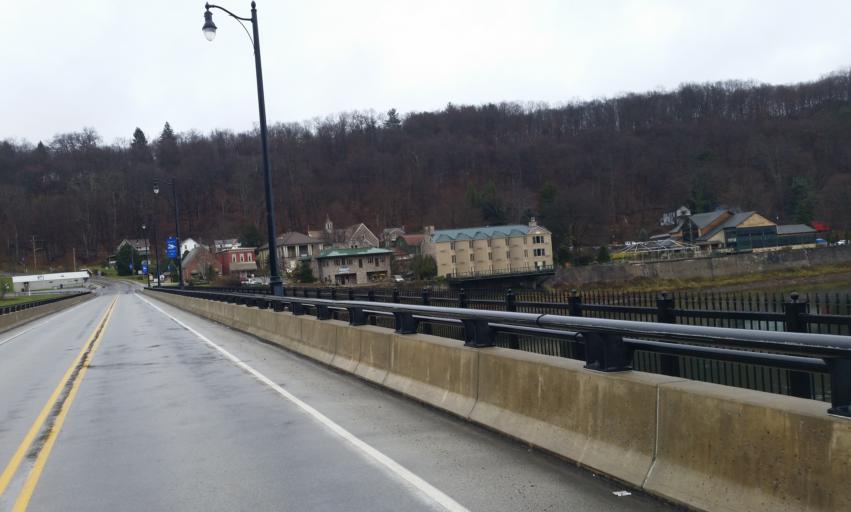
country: US
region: Pennsylvania
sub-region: Clarion County
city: Knox
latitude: 41.1398
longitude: -79.6816
